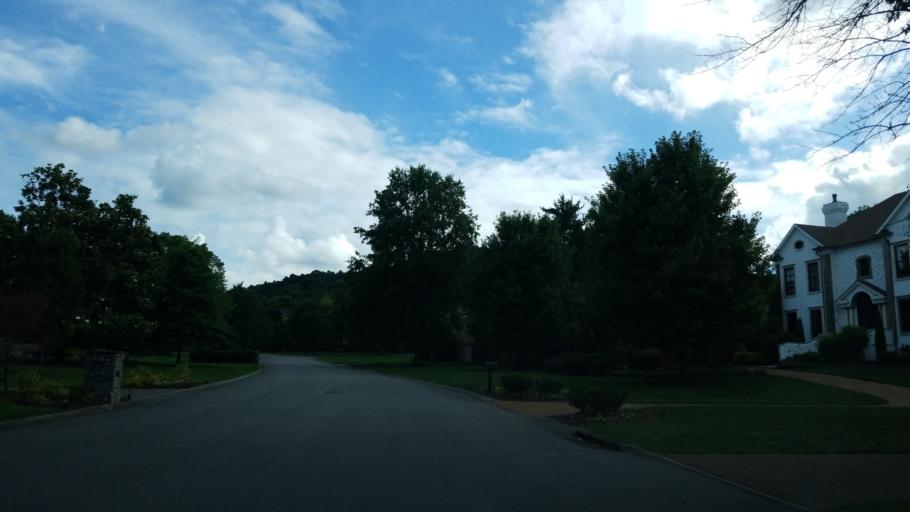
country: US
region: Tennessee
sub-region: Davidson County
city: Forest Hills
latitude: 36.0296
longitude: -86.8317
